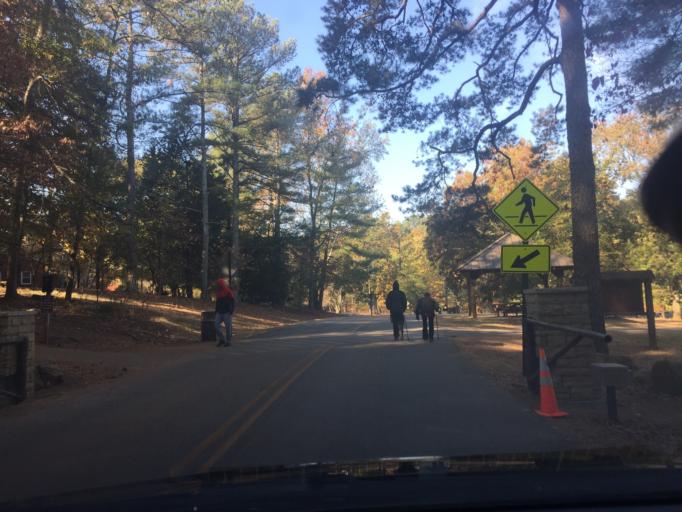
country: US
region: Georgia
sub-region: Cobb County
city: Marietta
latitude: 33.9825
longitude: -84.5779
